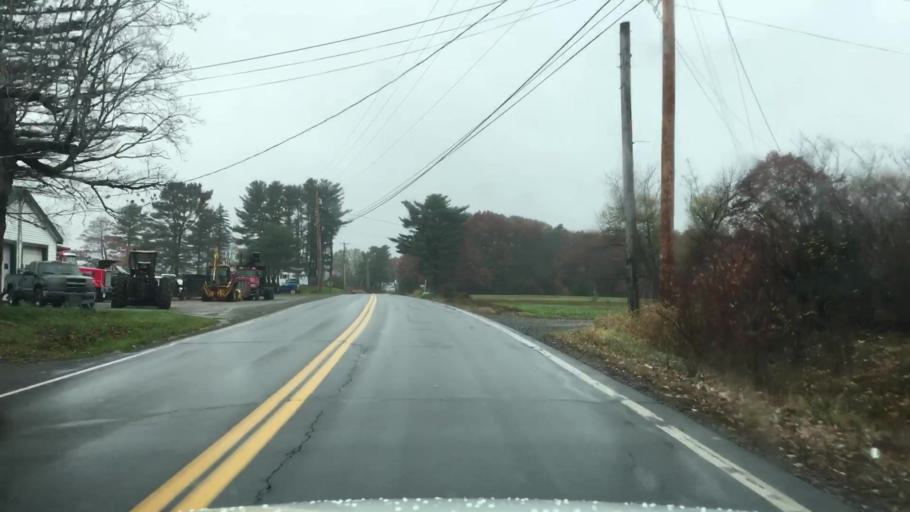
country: US
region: Maine
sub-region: Lincoln County
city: Waldoboro
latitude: 44.1258
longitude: -69.4122
